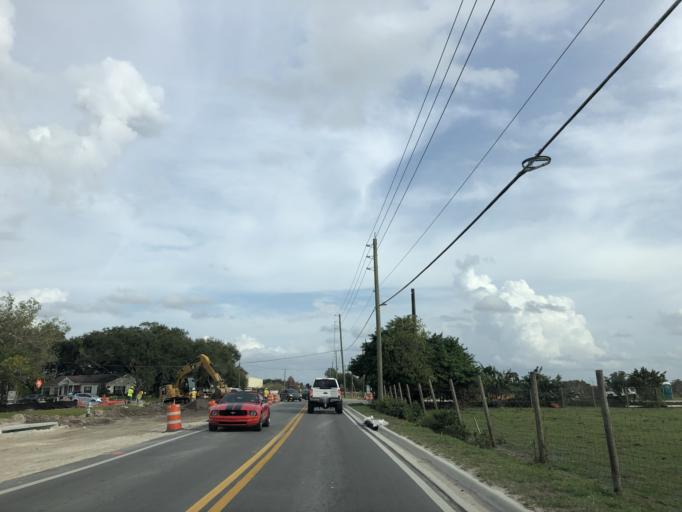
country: US
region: Florida
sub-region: Osceola County
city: Buenaventura Lakes
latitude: 28.2786
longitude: -81.3582
